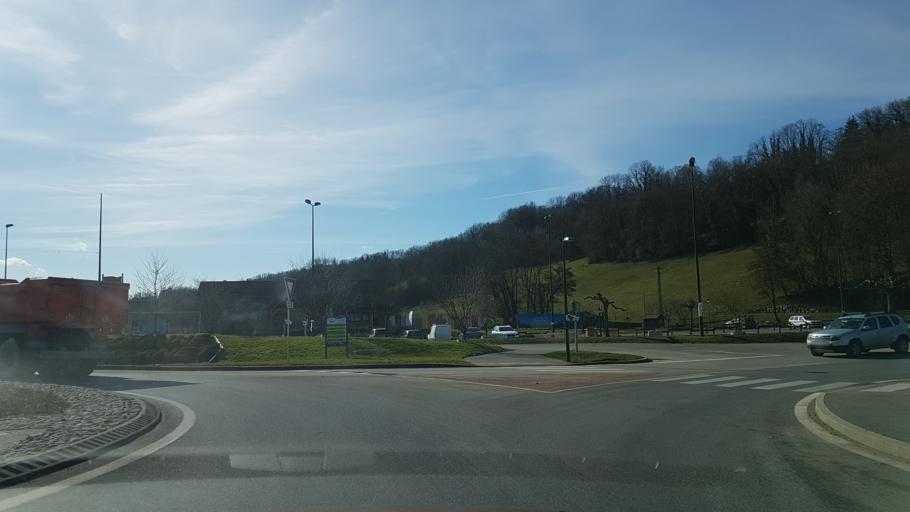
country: FR
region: Rhone-Alpes
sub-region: Departement de la Haute-Savoie
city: La Balme-de-Sillingy
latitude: 45.9718
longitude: 6.0324
